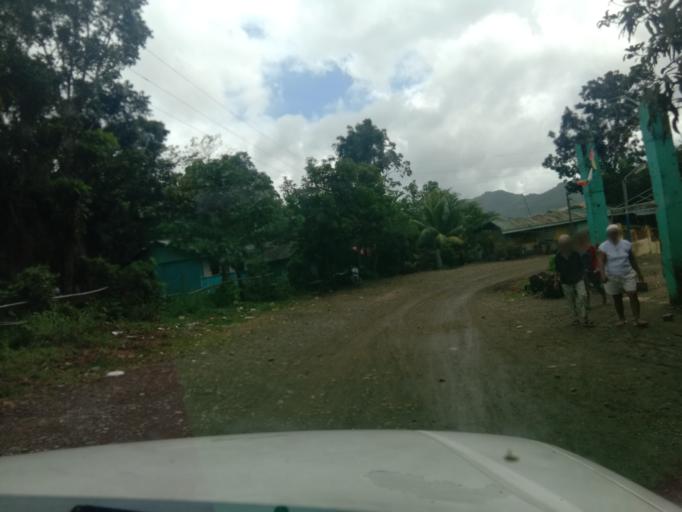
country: PH
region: Western Visayas
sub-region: Province of Capiz
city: Lantangan
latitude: 11.3663
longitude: 122.9072
